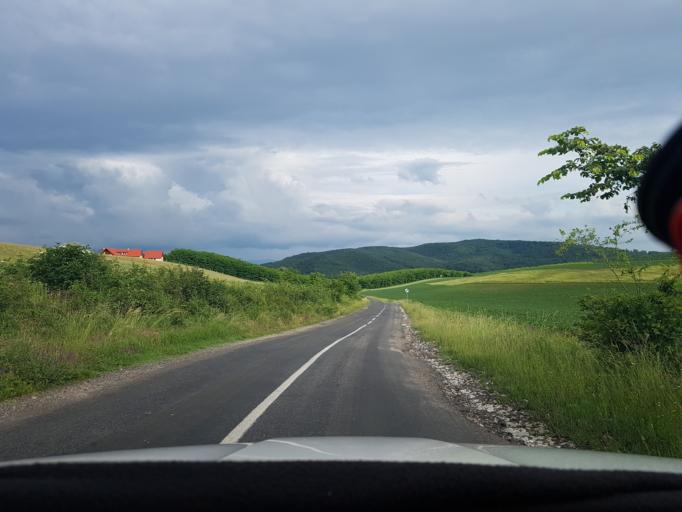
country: HU
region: Komarom-Esztergom
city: Nyergesujfalu
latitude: 47.7217
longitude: 18.5495
